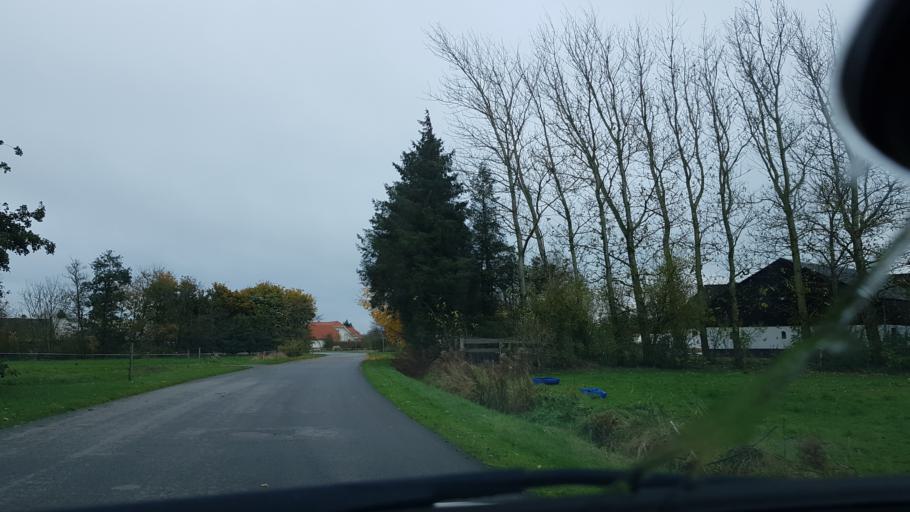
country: DK
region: South Denmark
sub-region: Tonder Kommune
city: Sherrebek
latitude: 55.2133
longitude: 8.8046
